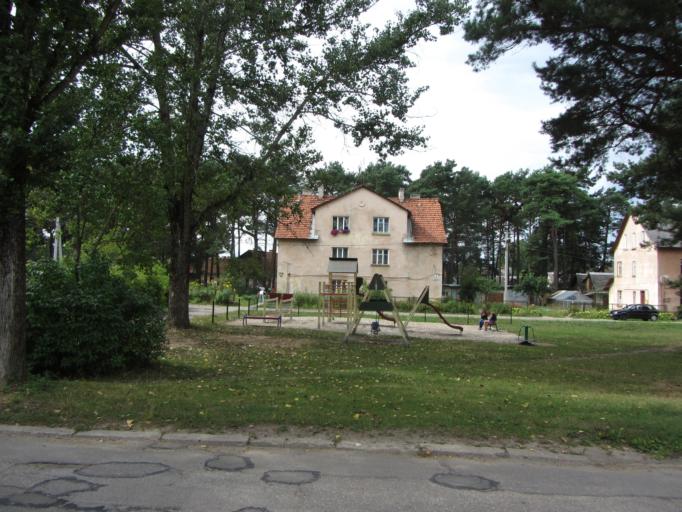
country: LT
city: Grigiskes
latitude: 54.6727
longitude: 25.0900
